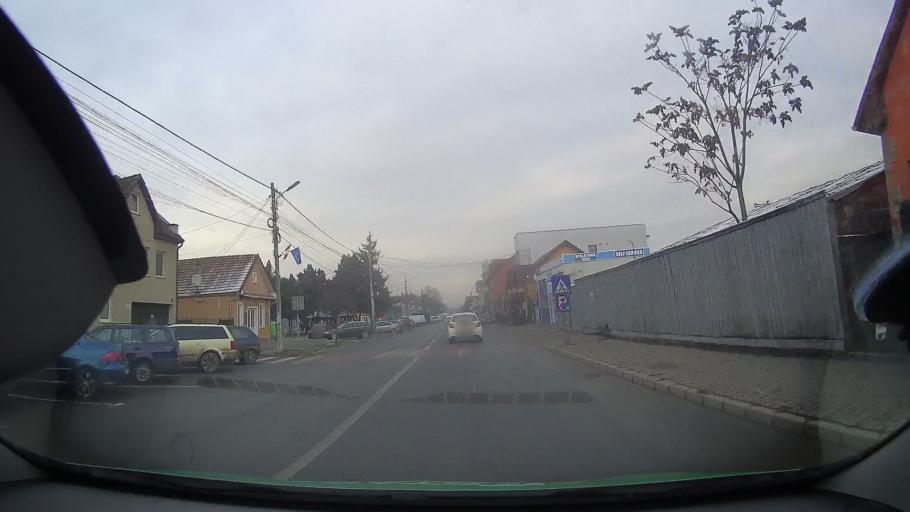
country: RO
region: Mures
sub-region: Comuna Ludus
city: Ludus
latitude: 46.4705
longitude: 24.0953
